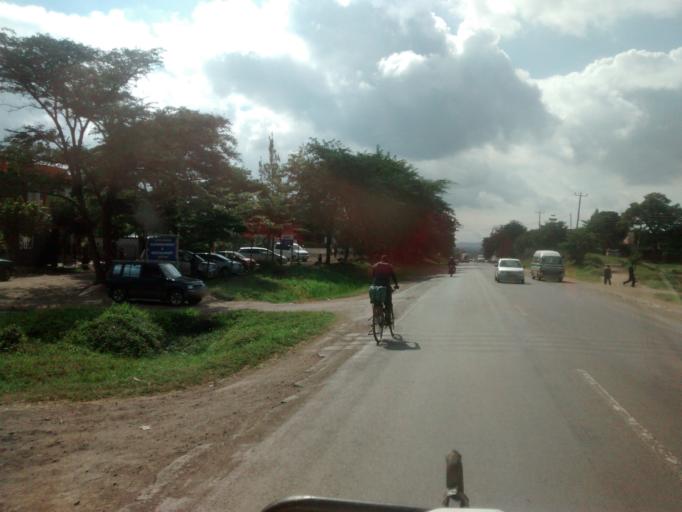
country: TZ
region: Arusha
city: Usa River
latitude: -3.3735
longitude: 36.8451
